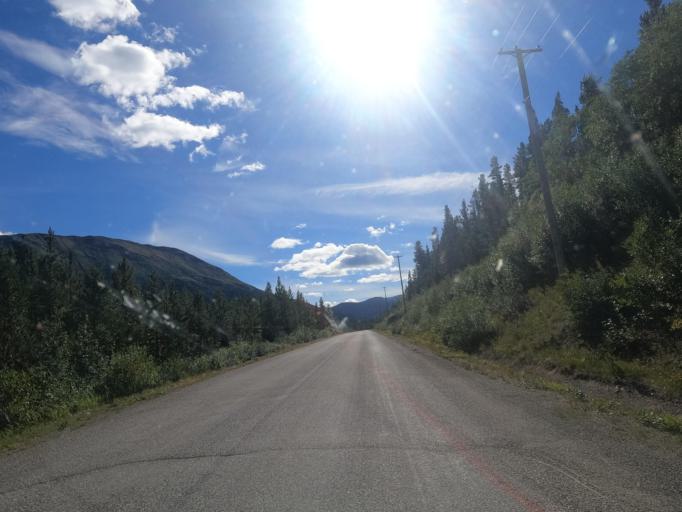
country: CA
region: Yukon
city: Watson Lake
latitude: 59.2812
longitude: -129.5464
